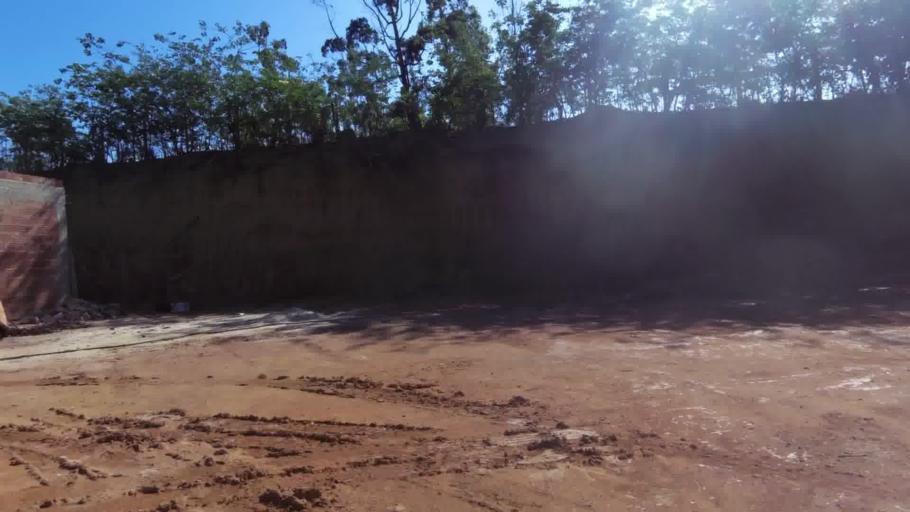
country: BR
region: Espirito Santo
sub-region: Piuma
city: Piuma
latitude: -20.8141
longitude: -40.6233
